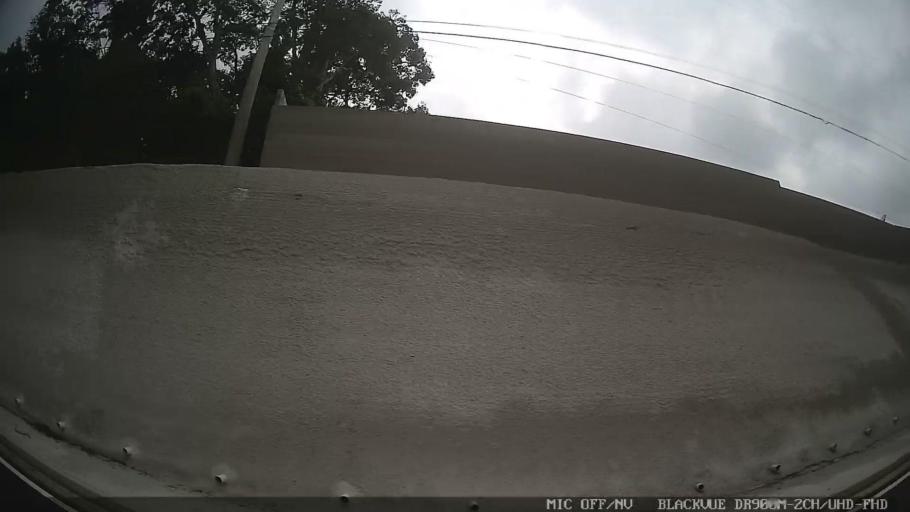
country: BR
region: Sao Paulo
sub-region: Aruja
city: Aruja
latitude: -23.4288
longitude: -46.2763
